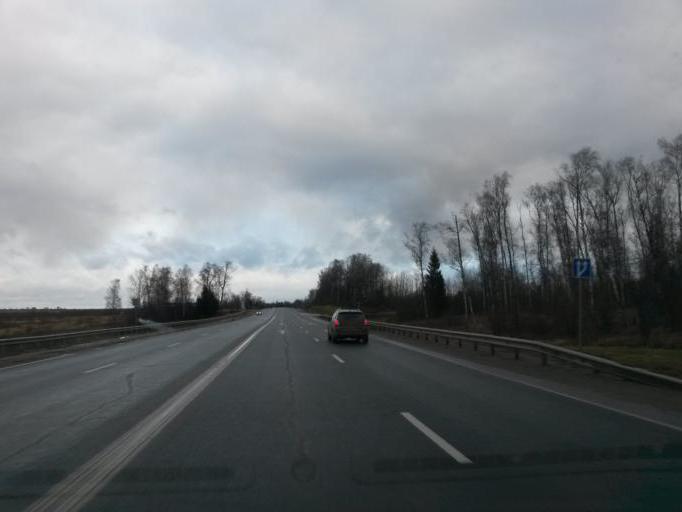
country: RU
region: Jaroslavl
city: Petrovsk
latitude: 57.0207
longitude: 39.2716
